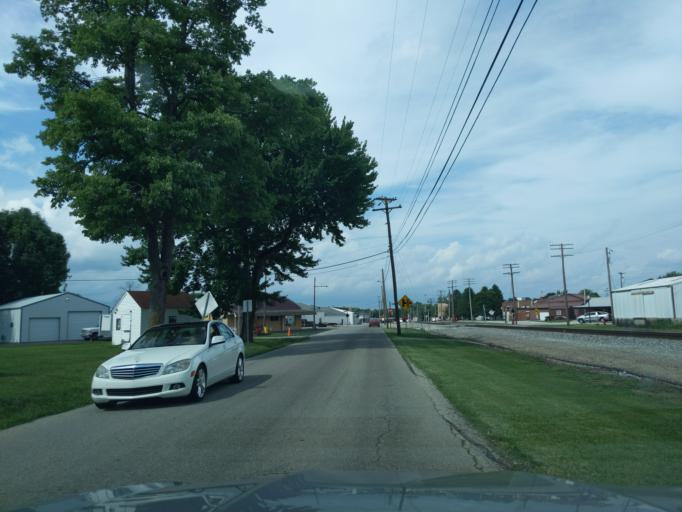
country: US
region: Indiana
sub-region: Ripley County
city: Osgood
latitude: 39.1281
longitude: -85.2944
